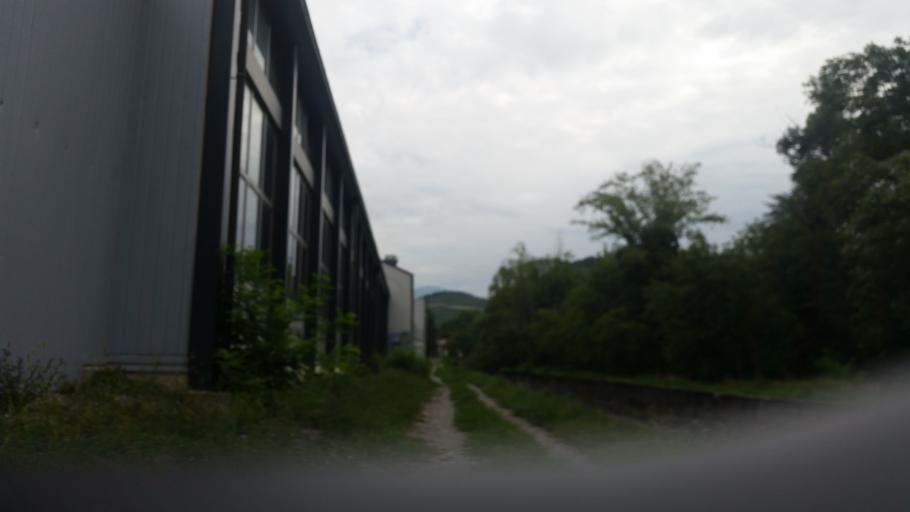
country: CH
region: Valais
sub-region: Conthey District
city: Conthey
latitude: 46.2232
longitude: 7.3105
